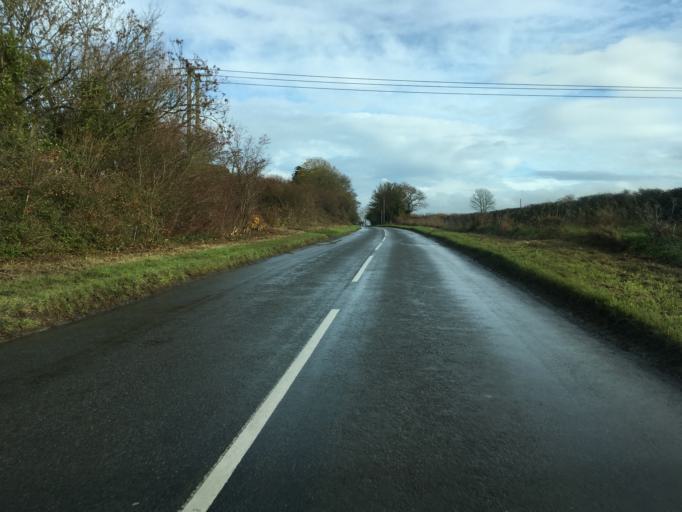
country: GB
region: England
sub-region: South Gloucestershire
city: Pucklechurch
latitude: 51.4891
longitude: -2.4126
